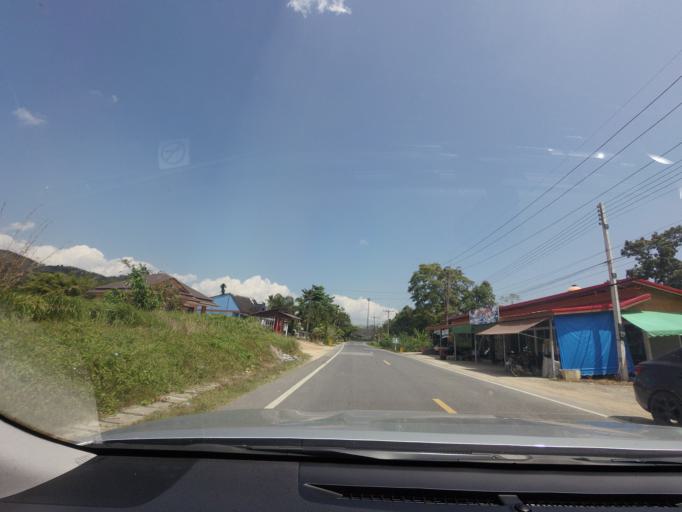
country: TH
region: Phangnga
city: Takua Thung
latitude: 8.2481
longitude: 98.3940
